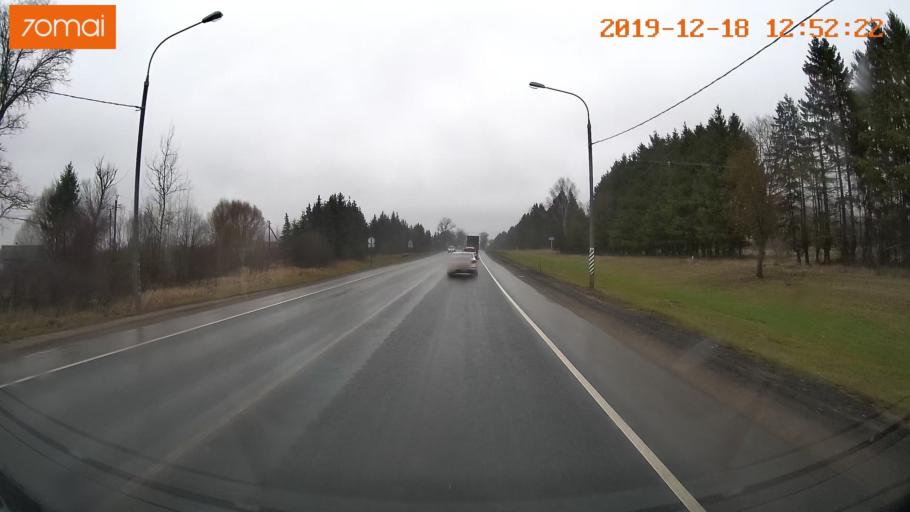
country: RU
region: Moskovskaya
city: Klin
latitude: 56.3108
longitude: 36.6871
